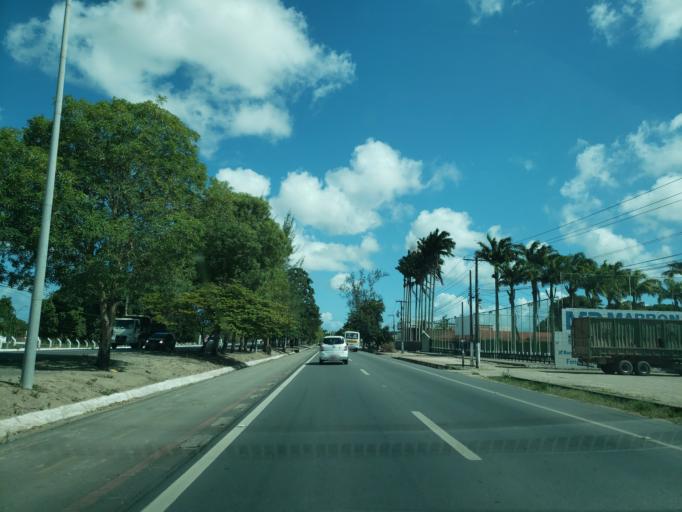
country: BR
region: Alagoas
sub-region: Satuba
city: Satuba
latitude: -9.5504
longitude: -35.7856
